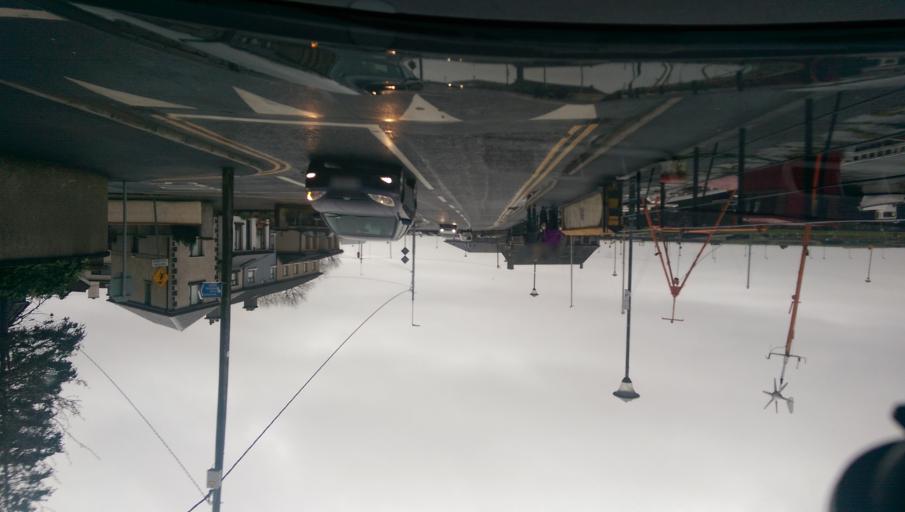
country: IE
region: Connaught
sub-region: County Galway
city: Gaillimh
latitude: 53.2685
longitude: -9.0553
